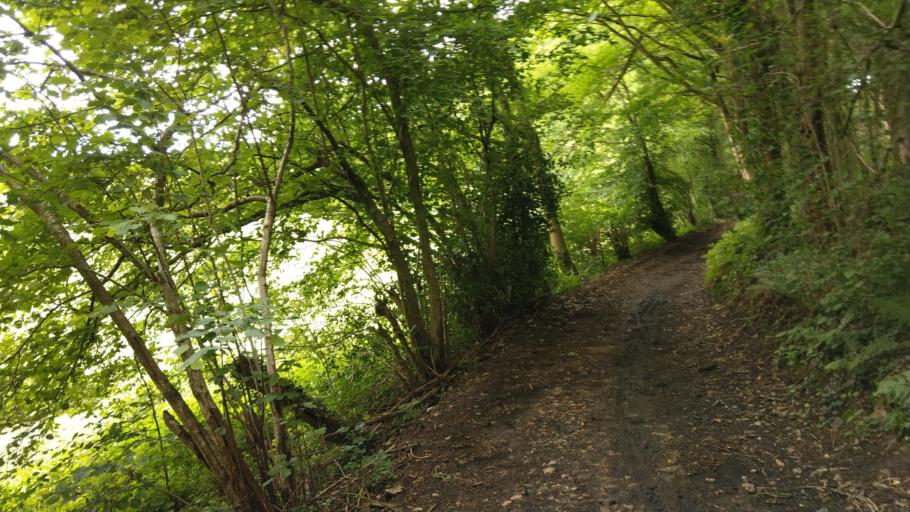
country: BE
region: Wallonia
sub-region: Province de Liege
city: La Calamine
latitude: 50.7427
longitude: 6.0118
